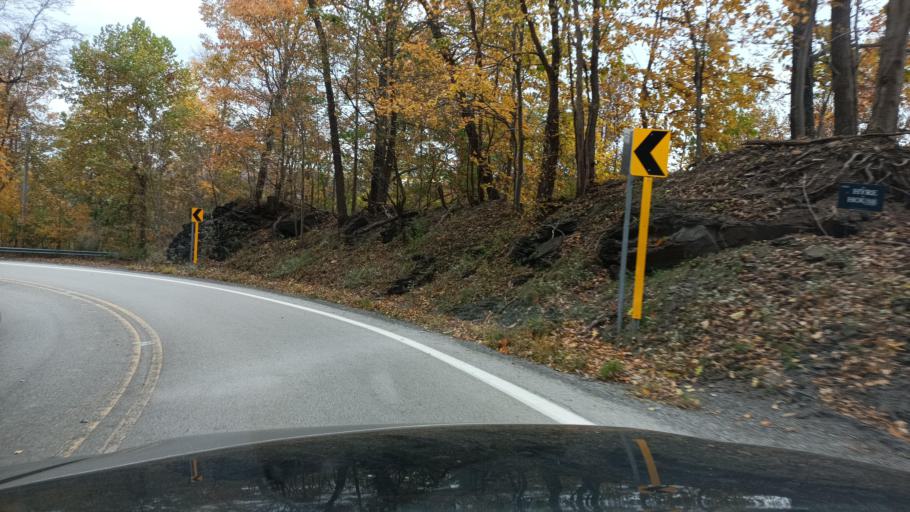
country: US
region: West Virginia
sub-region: Preston County
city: Terra Alta
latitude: 39.3004
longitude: -79.6136
